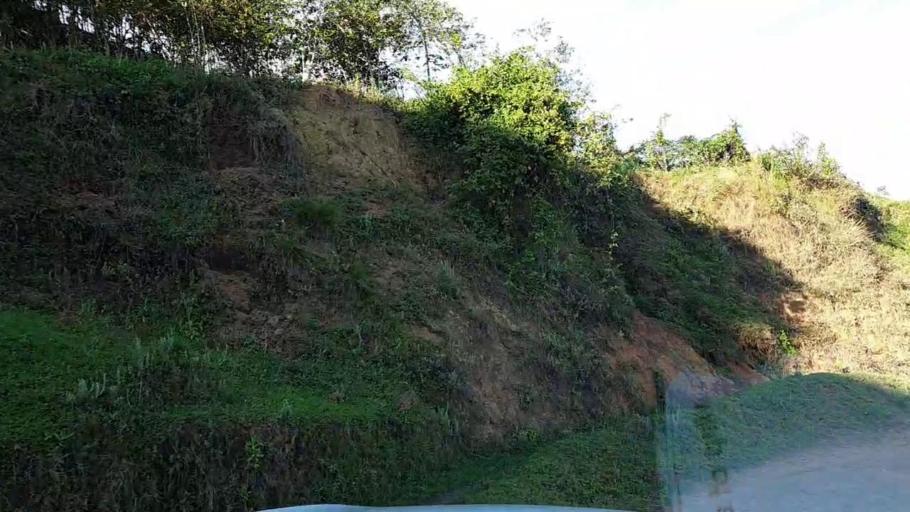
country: RW
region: Southern Province
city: Gikongoro
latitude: -2.4111
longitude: 29.5213
